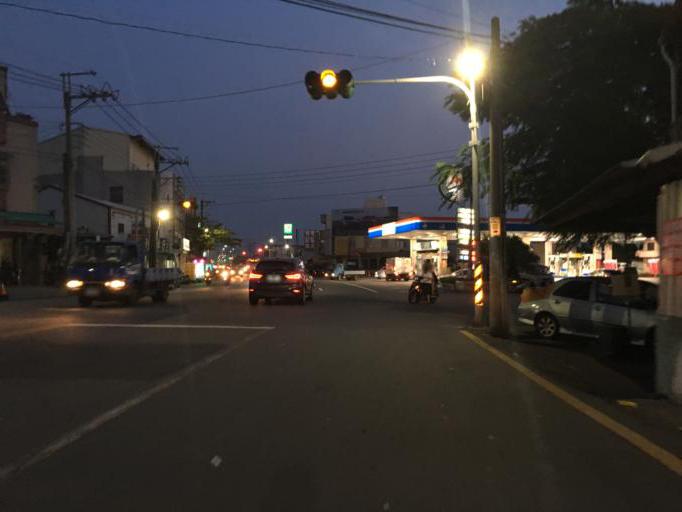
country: TW
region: Taiwan
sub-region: Chiayi
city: Taibao
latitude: 23.5514
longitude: 120.3473
